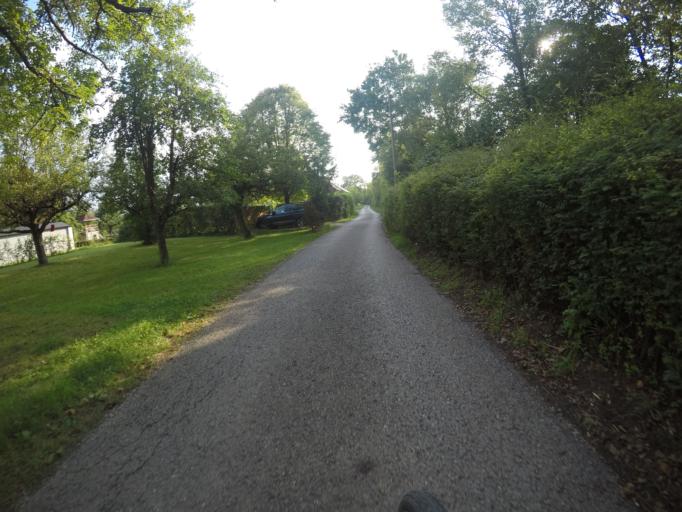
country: DE
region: Baden-Wuerttemberg
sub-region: Tuebingen Region
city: Pliezhausen
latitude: 48.5283
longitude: 9.2171
